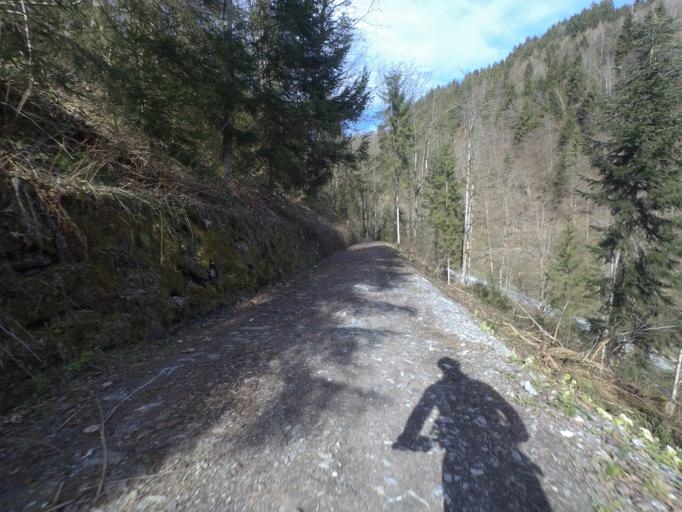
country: AT
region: Salzburg
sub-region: Politischer Bezirk Sankt Johann im Pongau
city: Sankt Veit im Pongau
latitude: 47.3284
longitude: 13.1342
